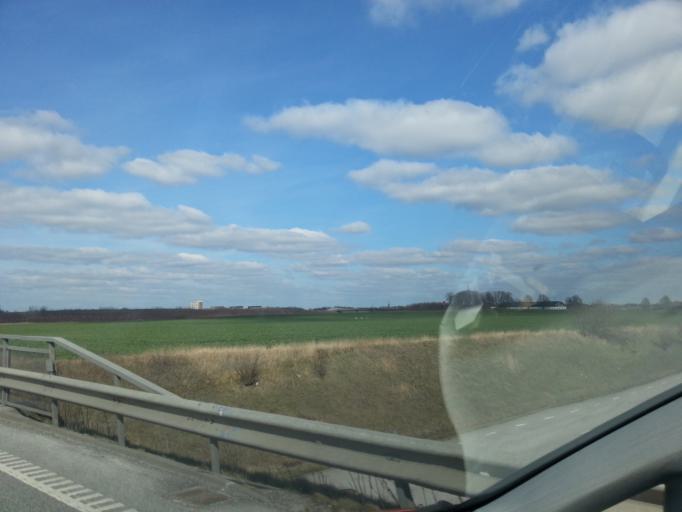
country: SE
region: Skane
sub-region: Malmo
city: Tygelsjo
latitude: 55.5426
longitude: 13.0049
